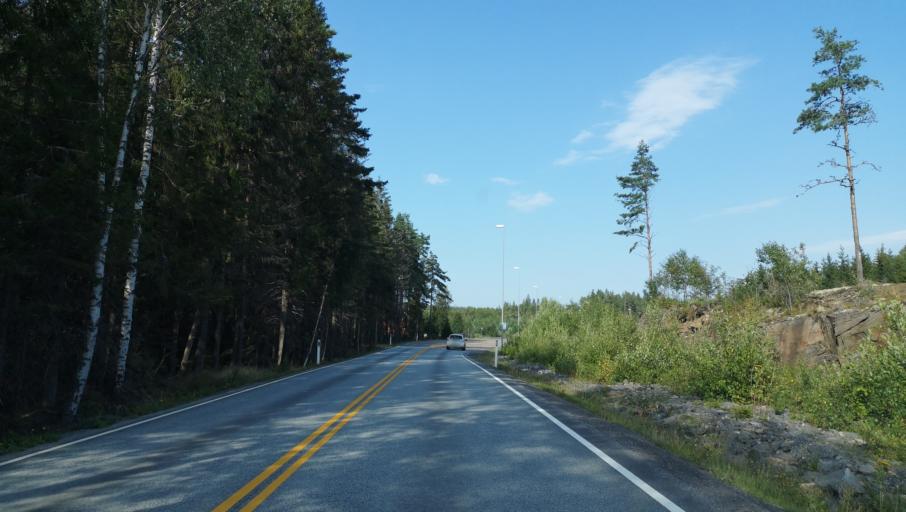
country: NO
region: Ostfold
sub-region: Valer
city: Kirkebygda
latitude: 59.4809
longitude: 10.7941
